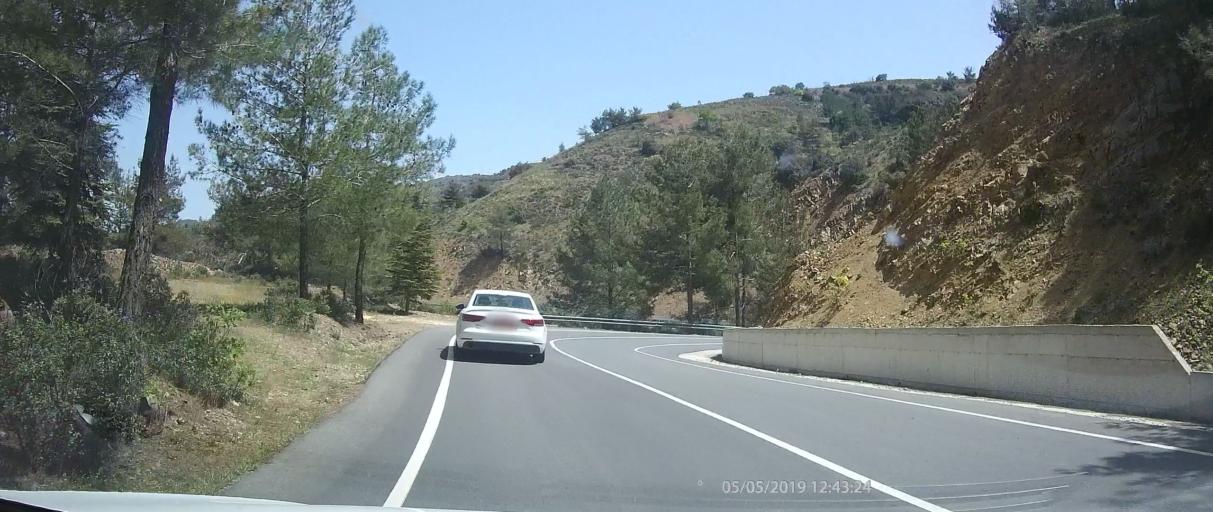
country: CY
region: Lefkosia
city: Kakopetria
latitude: 34.9682
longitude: 32.8139
